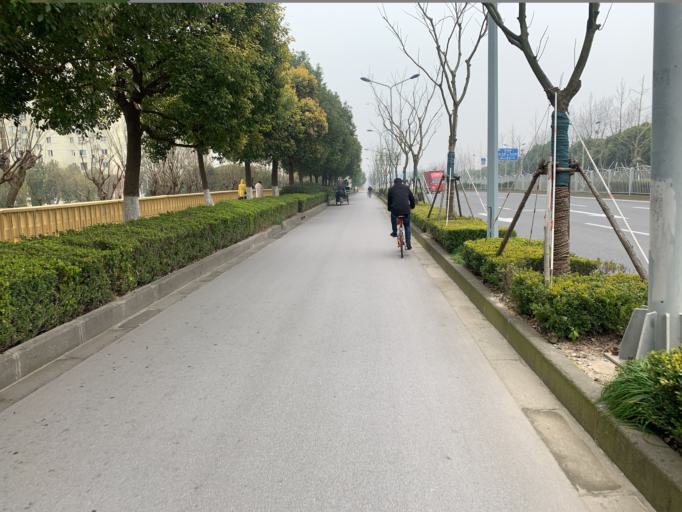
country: CN
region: Shanghai Shi
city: Huamu
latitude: 31.2433
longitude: 121.6213
